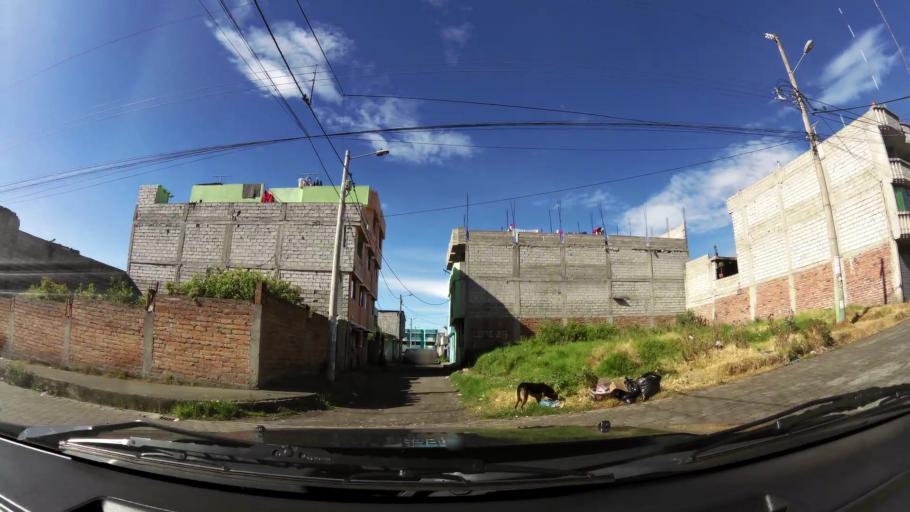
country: EC
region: Pichincha
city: Quito
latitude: -0.3076
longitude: -78.5668
